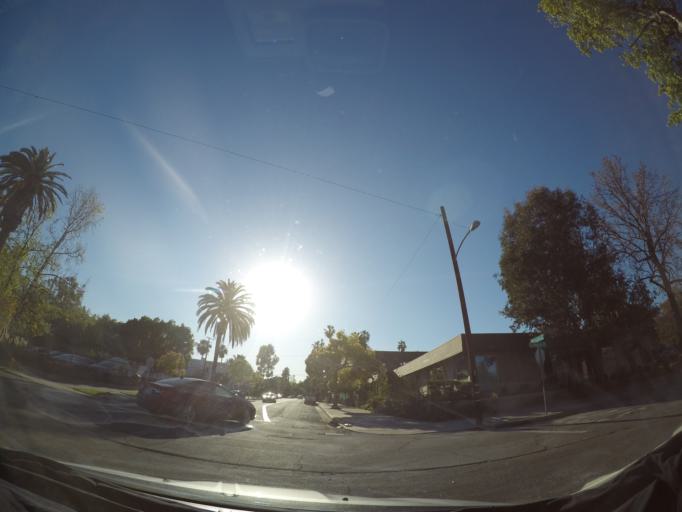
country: US
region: California
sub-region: Los Angeles County
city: South Pasadena
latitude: 34.1149
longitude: -118.1517
